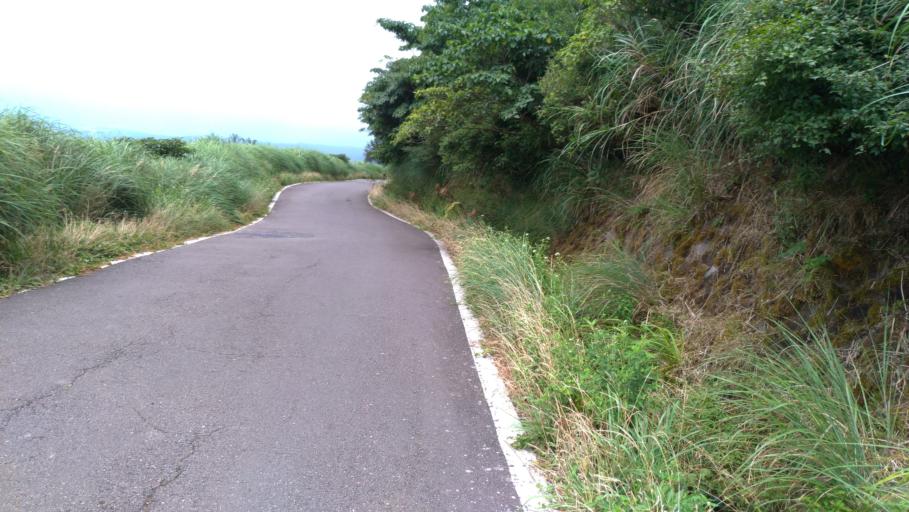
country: TW
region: Taipei
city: Taipei
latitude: 25.1794
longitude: 121.5208
